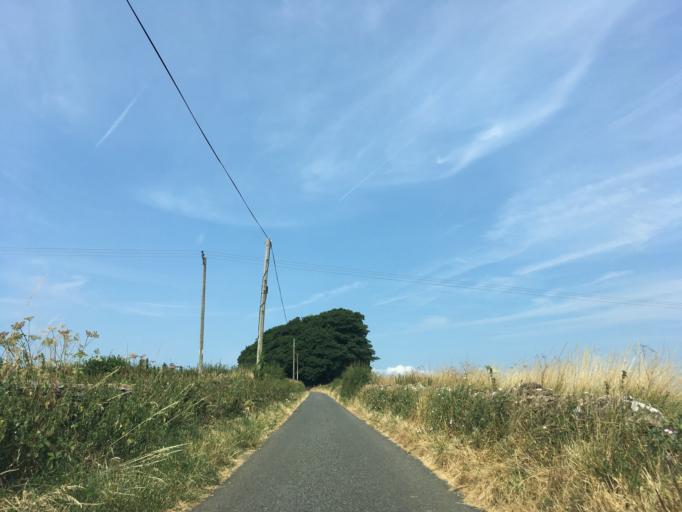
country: GB
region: England
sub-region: Gloucestershire
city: Nailsworth
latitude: 51.6667
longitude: -2.2696
